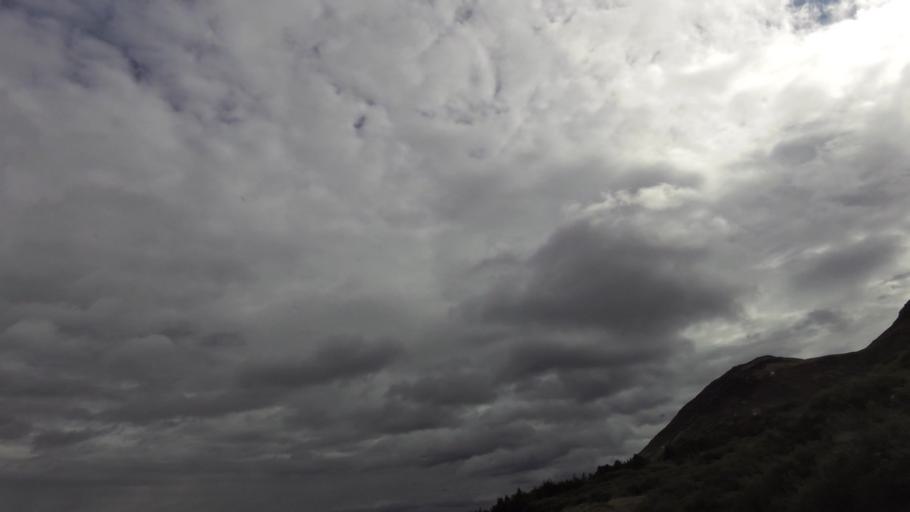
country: IS
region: West
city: Stykkisholmur
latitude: 65.5202
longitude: -22.1158
